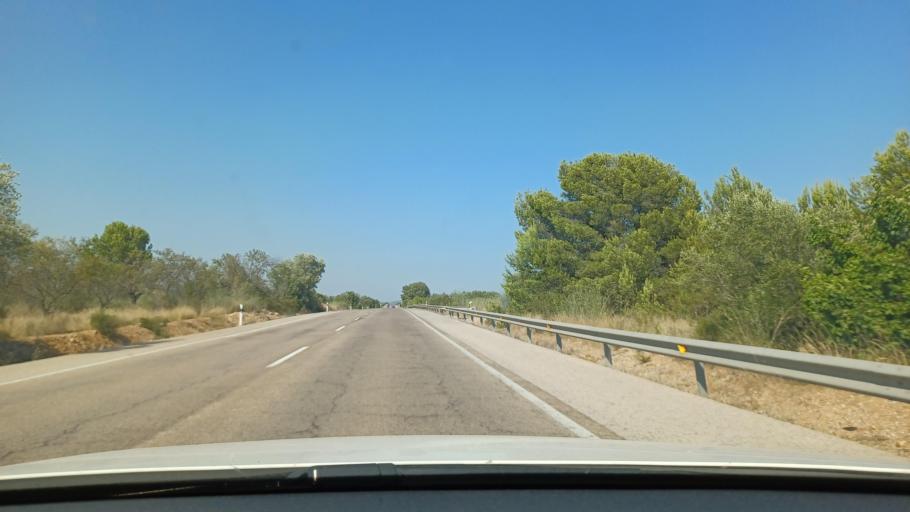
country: ES
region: Valencia
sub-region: Provincia de Castello
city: Alcala de Xivert
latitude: 40.3235
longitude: 0.2420
